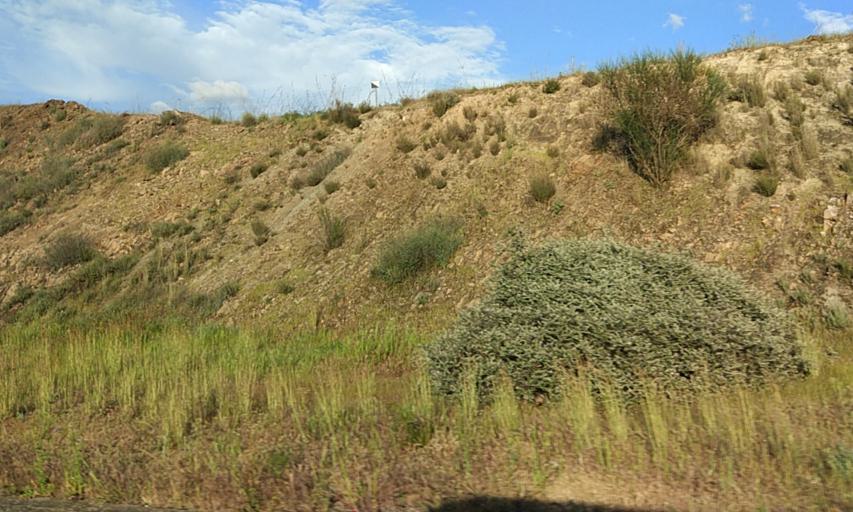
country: ES
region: Extremadura
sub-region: Provincia de Badajoz
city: Badajoz
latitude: 38.9094
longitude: -6.9938
